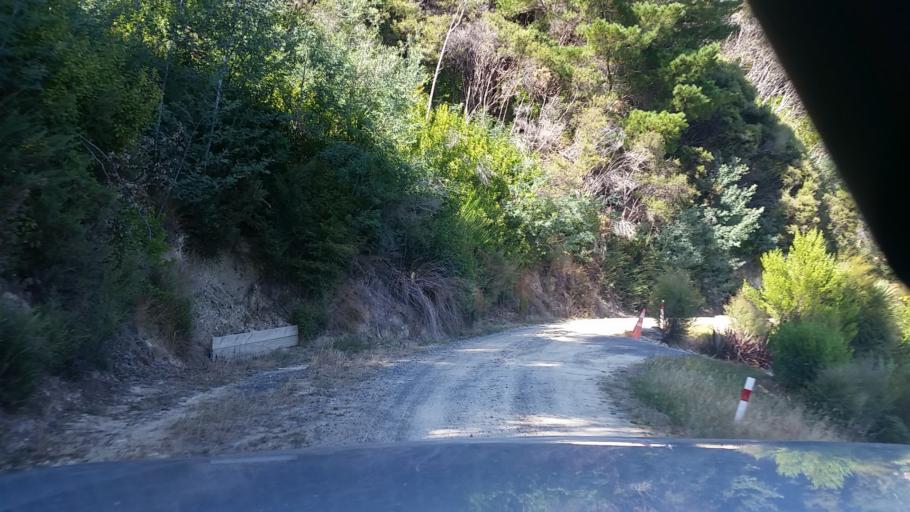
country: NZ
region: Marlborough
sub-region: Marlborough District
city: Picton
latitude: -41.3058
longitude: 174.1754
